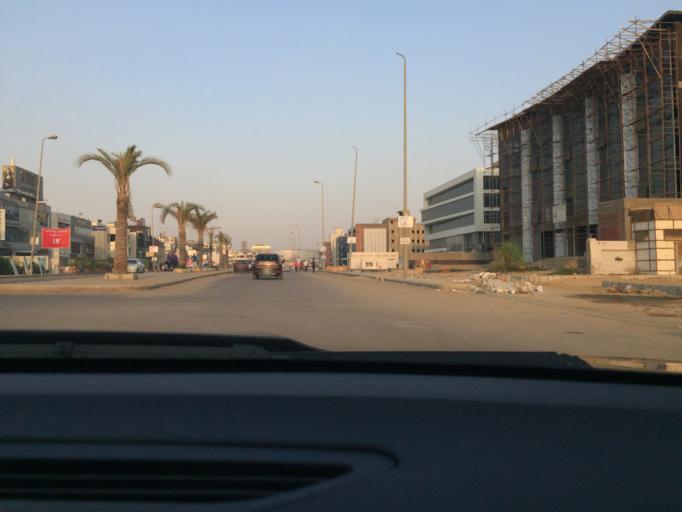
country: EG
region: Muhafazat al Qahirah
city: Cairo
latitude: 30.0183
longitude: 31.4190
